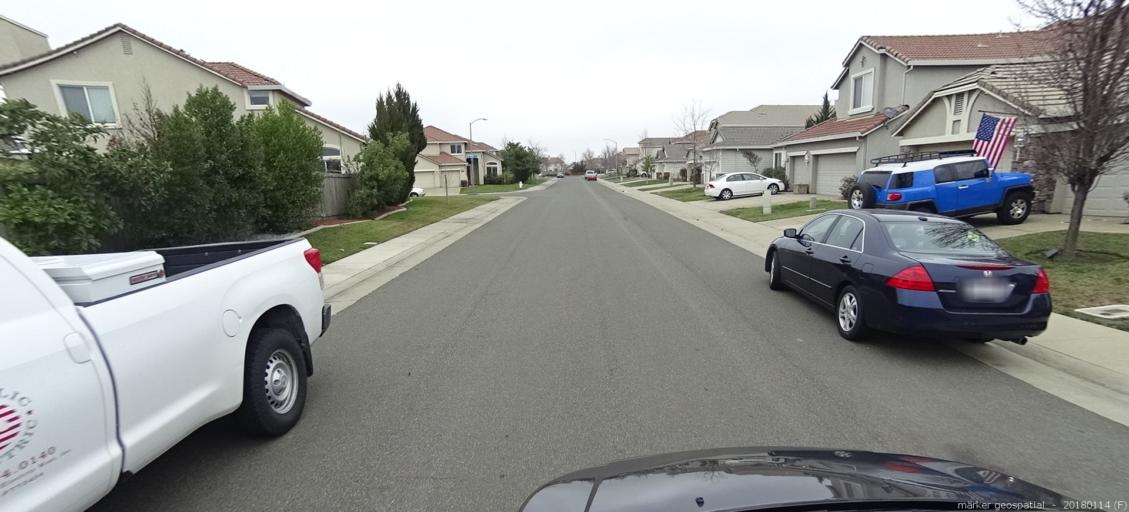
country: US
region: California
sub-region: Sacramento County
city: Gold River
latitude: 38.5474
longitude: -121.2343
